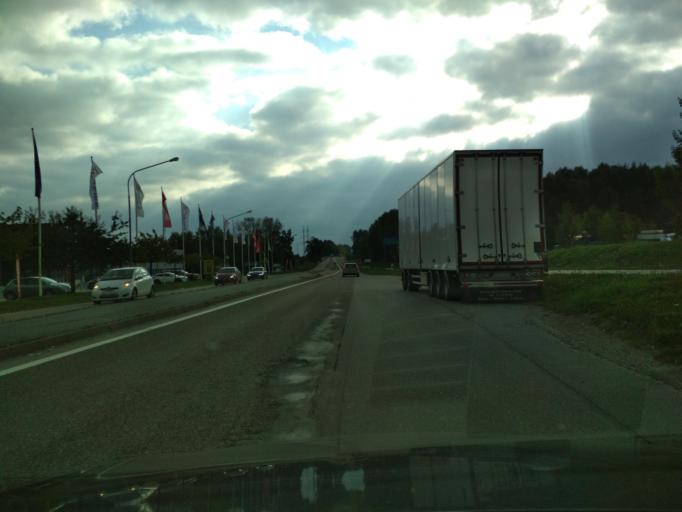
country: SE
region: Stockholm
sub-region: Upplands Vasby Kommun
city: Upplands Vaesby
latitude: 59.4989
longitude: 17.9215
